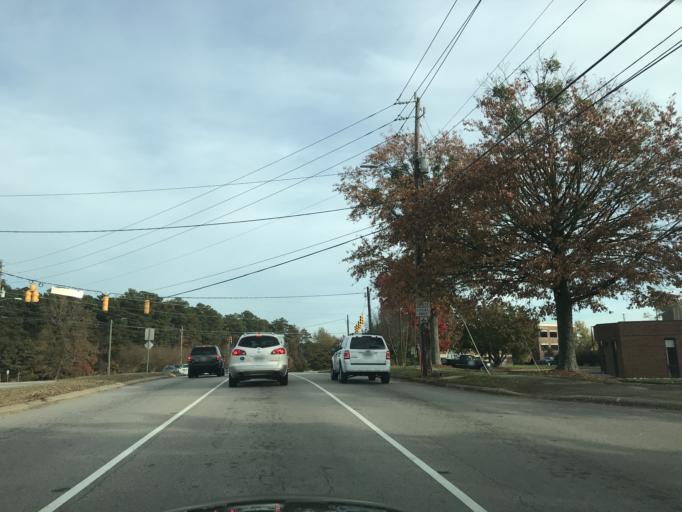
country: US
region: North Carolina
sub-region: Wake County
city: West Raleigh
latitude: 35.9010
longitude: -78.6529
